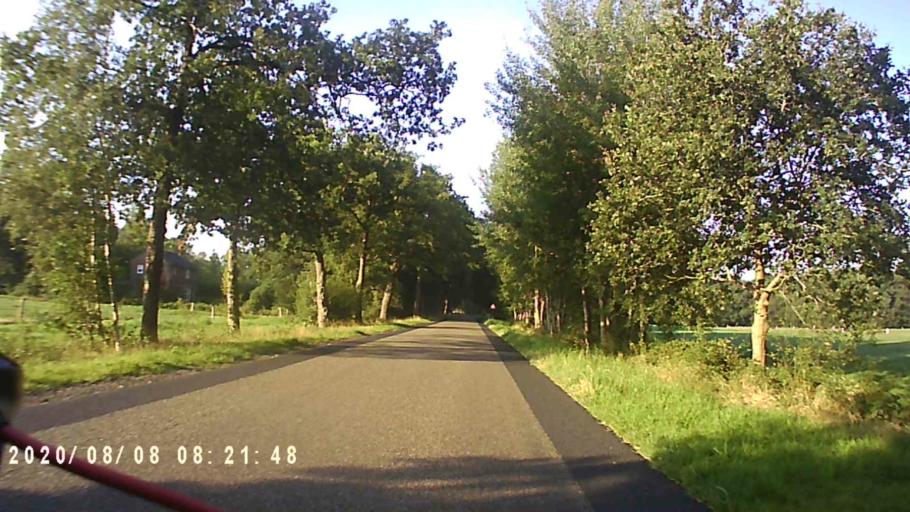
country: NL
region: Groningen
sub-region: Gemeente Leek
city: Leek
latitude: 53.0922
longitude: 6.3136
